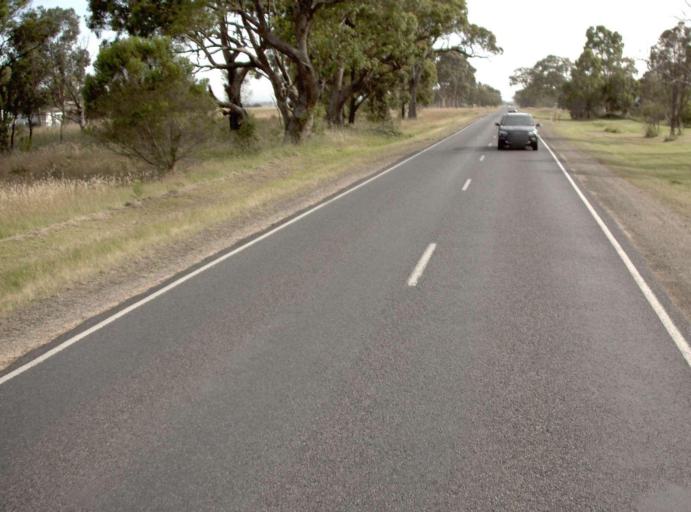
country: AU
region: Victoria
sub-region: Latrobe
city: Traralgon
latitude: -38.0670
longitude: 146.6174
